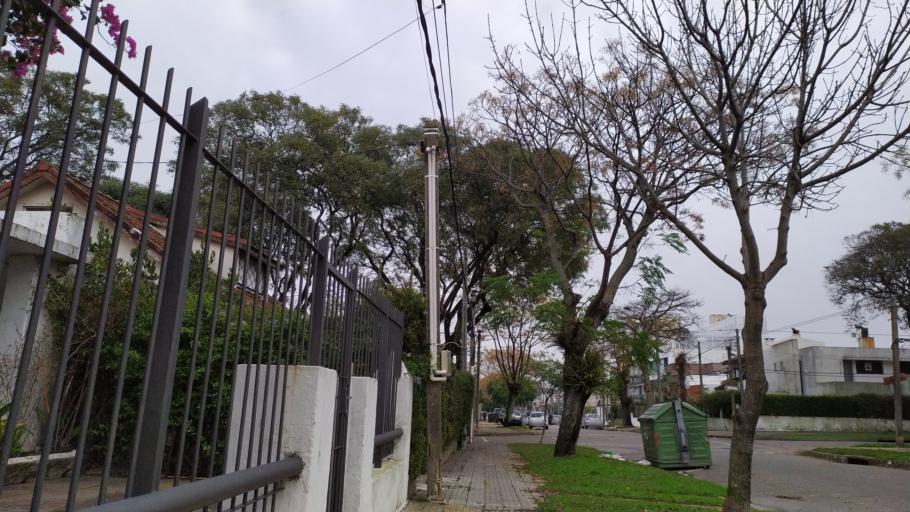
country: UY
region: Canelones
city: Paso de Carrasco
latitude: -34.8940
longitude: -56.0993
